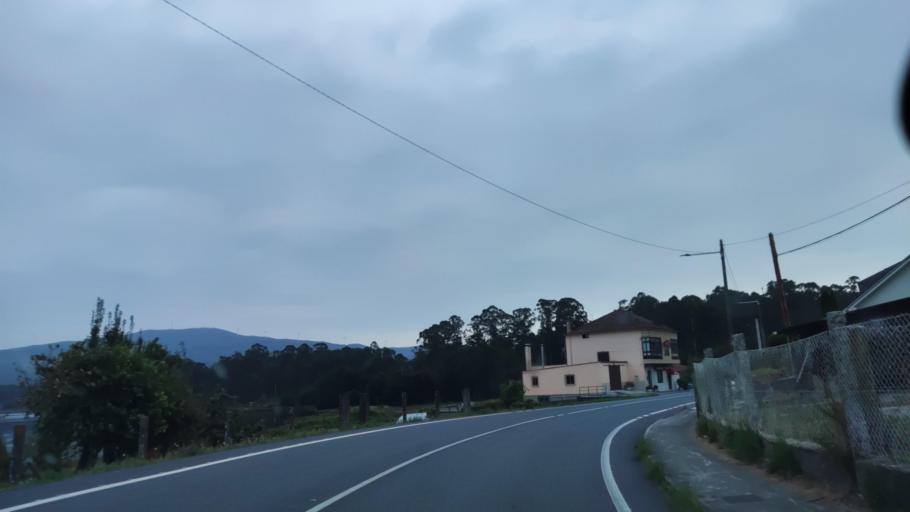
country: ES
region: Galicia
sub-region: Provincia de Pontevedra
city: Catoira
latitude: 42.6867
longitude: -8.7325
